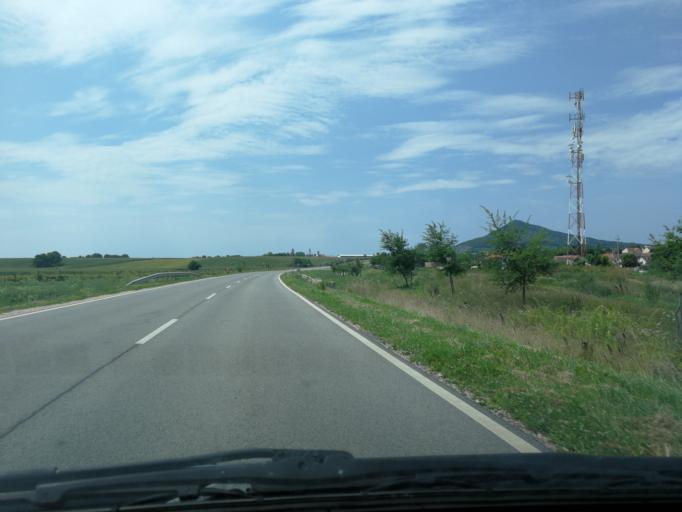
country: HU
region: Baranya
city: Villany
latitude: 45.8635
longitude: 18.4602
